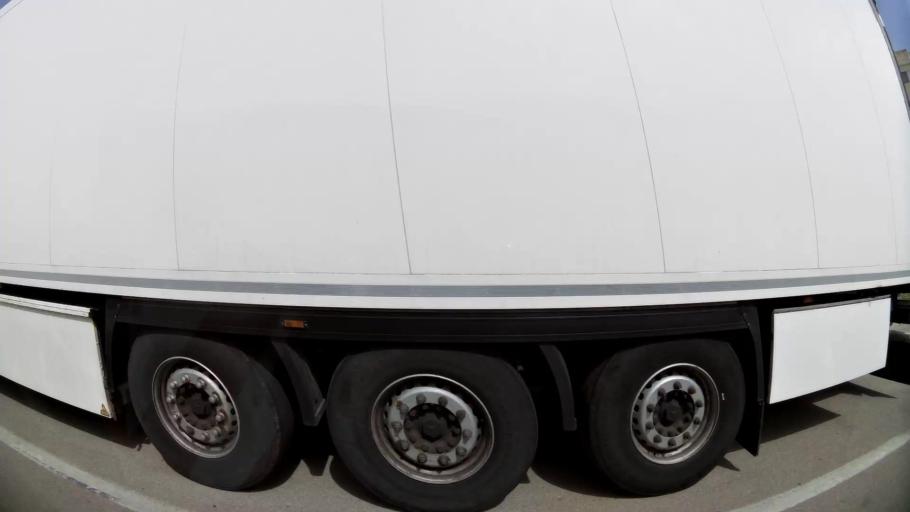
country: MA
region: Tanger-Tetouan
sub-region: Tanger-Assilah
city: Boukhalef
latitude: 35.7367
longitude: -5.8741
